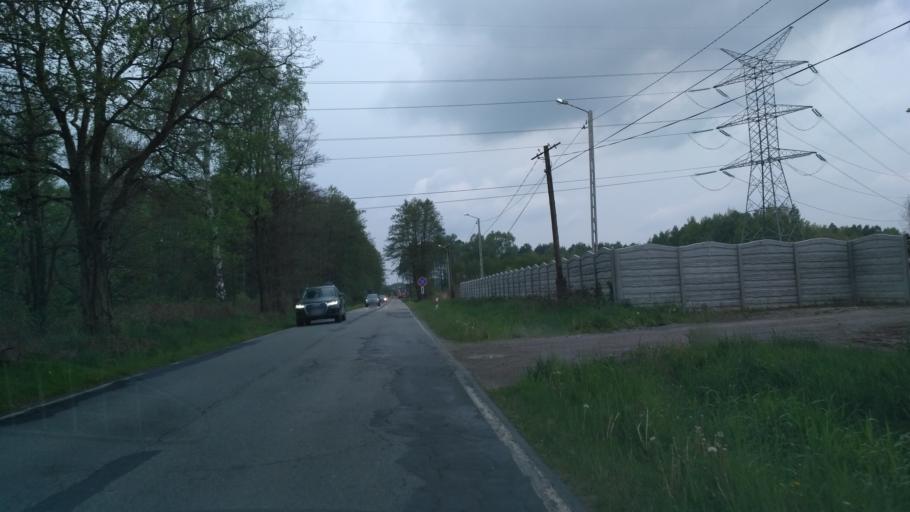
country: PL
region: Subcarpathian Voivodeship
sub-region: Powiat kolbuszowski
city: Kolbuszowa
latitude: 50.1868
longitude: 21.7620
